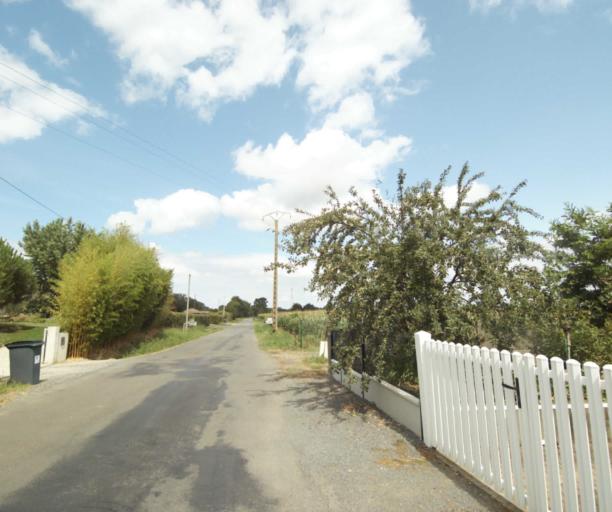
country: FR
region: Pays de la Loire
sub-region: Departement de la Sarthe
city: Sable-sur-Sarthe
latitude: 47.8581
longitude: -0.3552
